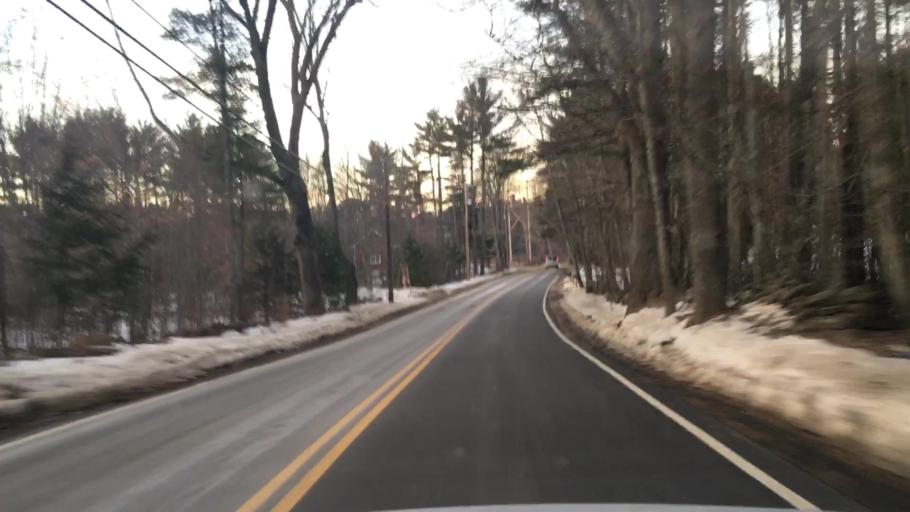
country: US
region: Maine
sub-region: York County
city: Lebanon
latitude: 43.4317
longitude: -70.8819
